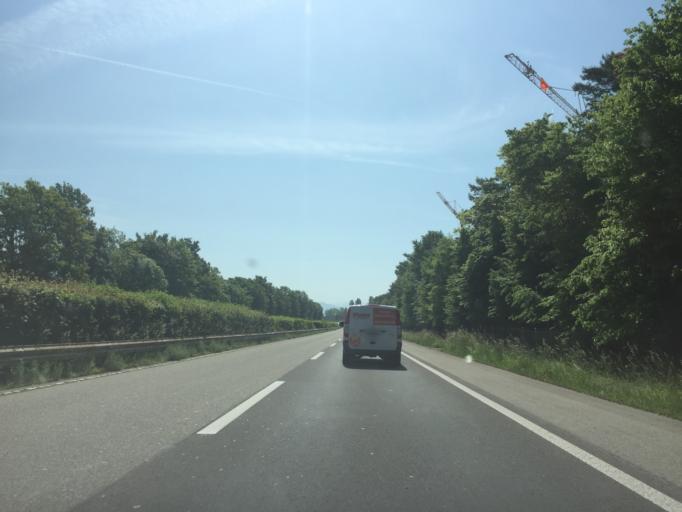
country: CH
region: Vaud
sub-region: Ouest Lausannois District
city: Prilly
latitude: 46.5212
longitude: 6.5917
